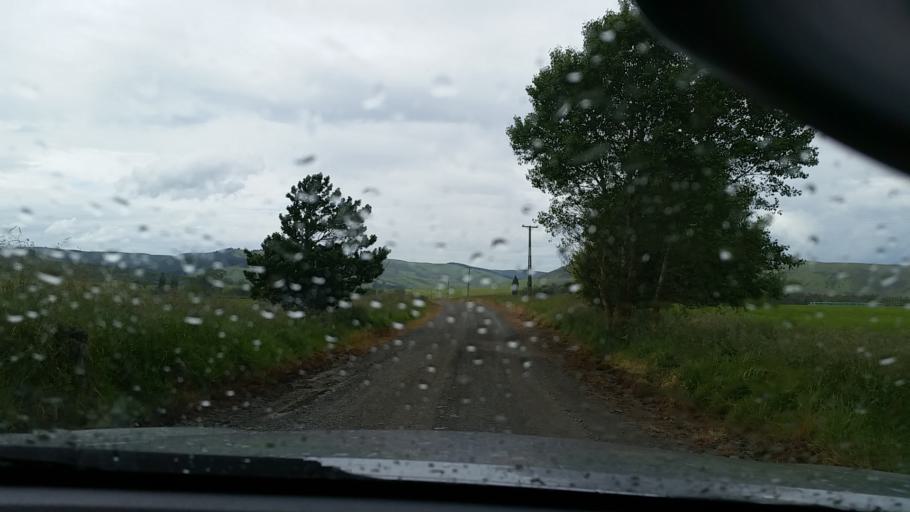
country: NZ
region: Southland
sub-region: Southland District
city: Winton
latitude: -45.9473
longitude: 168.1280
